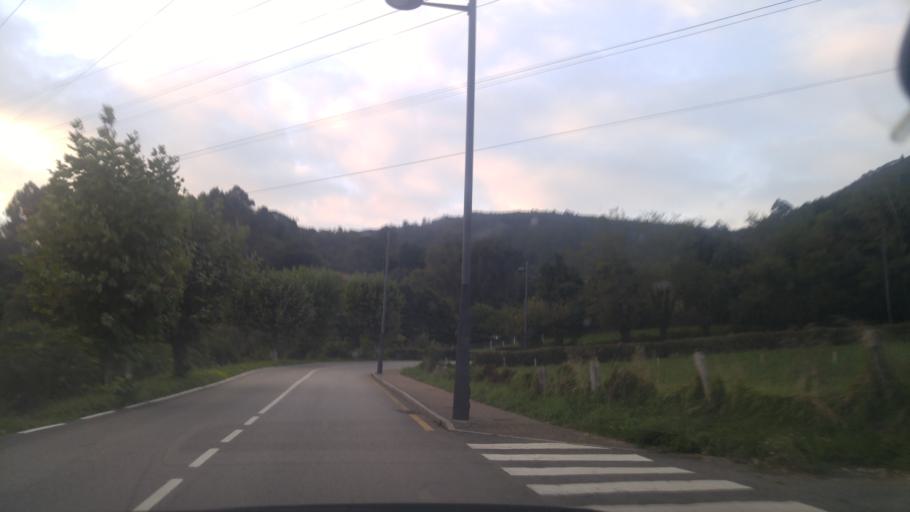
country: ES
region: Asturias
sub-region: Province of Asturias
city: Oviedo
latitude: 43.3769
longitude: -5.8662
